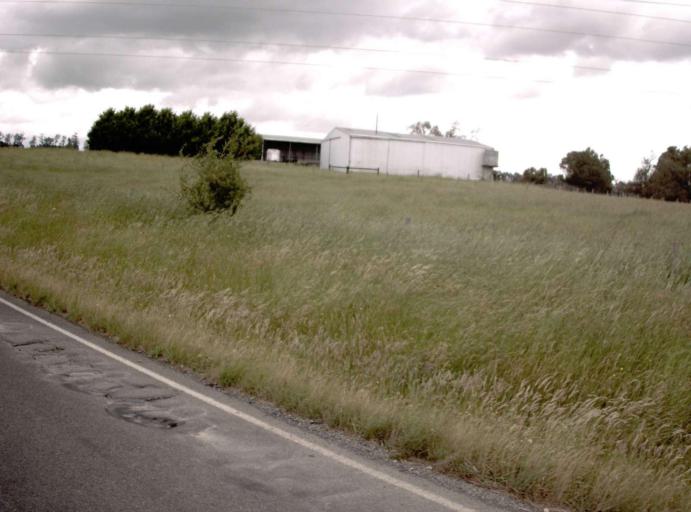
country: AU
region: Victoria
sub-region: Baw Baw
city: Warragul
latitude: -38.1159
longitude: 145.9783
